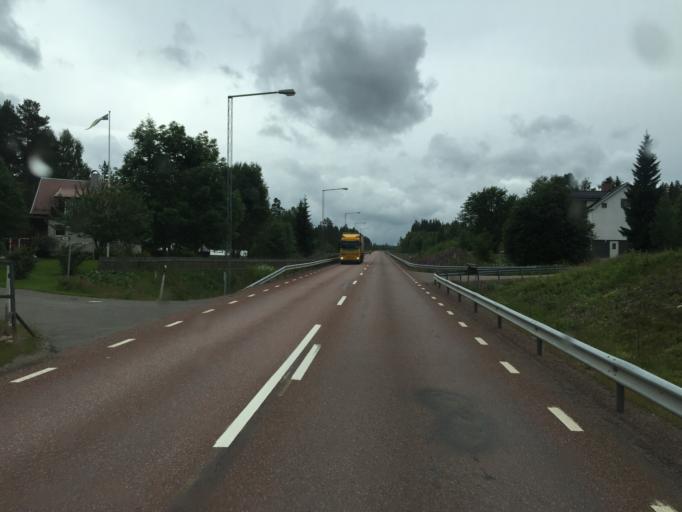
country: SE
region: Dalarna
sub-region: Malung-Saelens kommun
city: Malung
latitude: 60.6730
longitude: 13.6992
